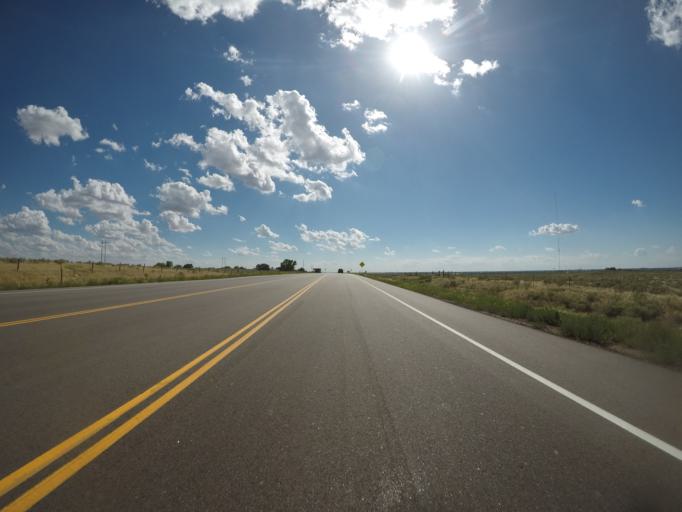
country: US
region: Colorado
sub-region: Logan County
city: Sterling
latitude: 40.6259
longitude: -103.1563
